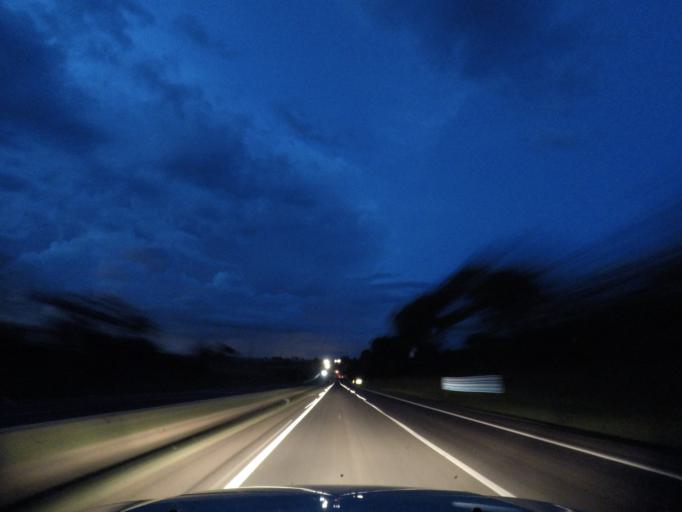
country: BR
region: Minas Gerais
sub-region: Uberlandia
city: Uberlandia
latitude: -19.2332
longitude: -48.1420
